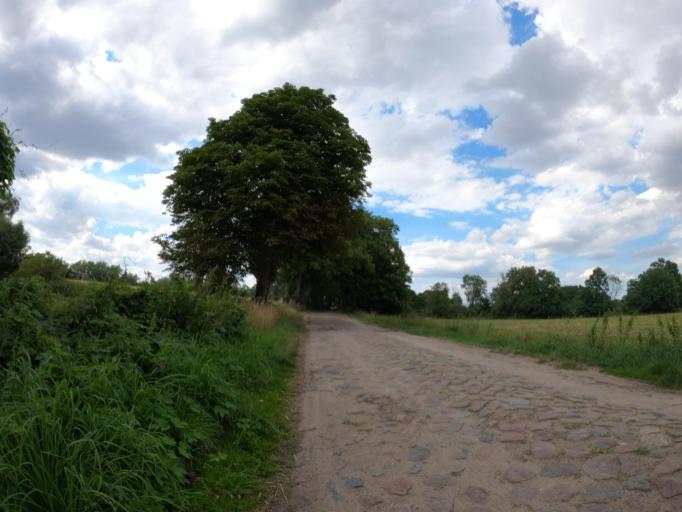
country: DE
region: Mecklenburg-Vorpommern
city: Woldegk
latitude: 53.4059
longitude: 13.6213
